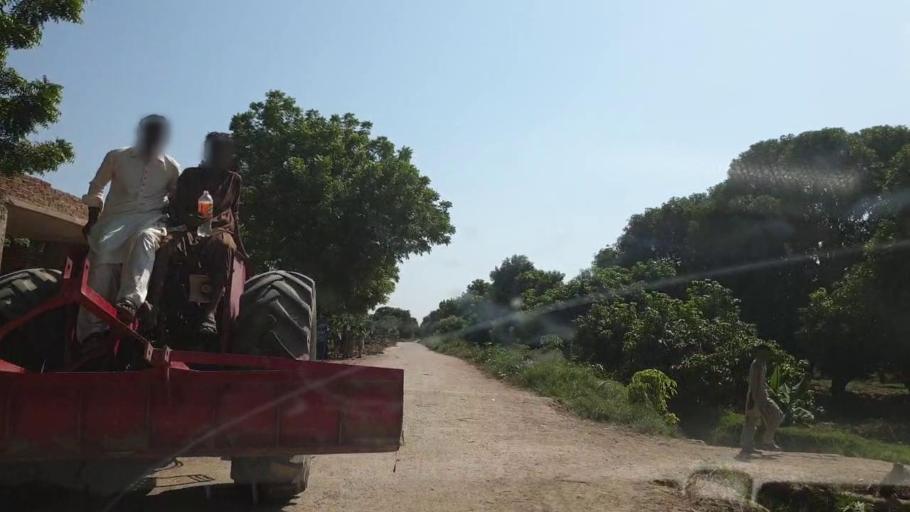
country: PK
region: Sindh
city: Tando Jam
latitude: 25.4109
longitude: 68.5821
